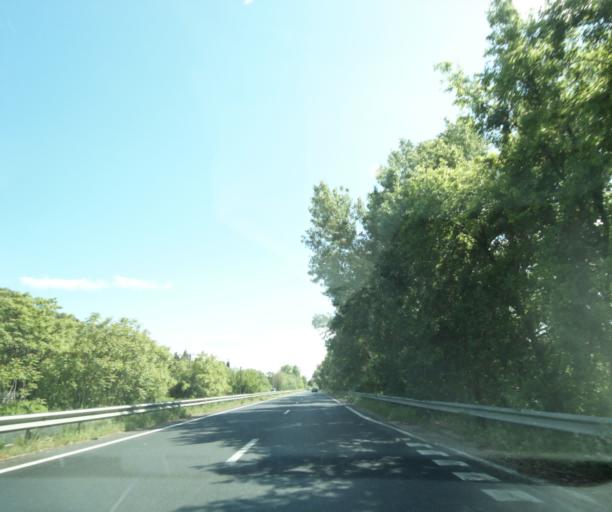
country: FR
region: Languedoc-Roussillon
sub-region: Departement de l'Herault
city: Juvignac
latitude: 43.6014
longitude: 3.8197
